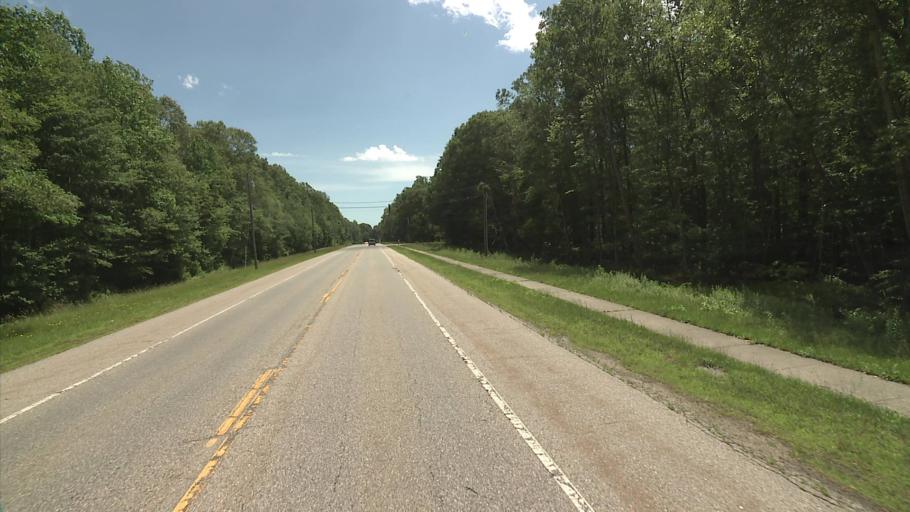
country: US
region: Connecticut
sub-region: New London County
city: Mystic
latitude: 41.3616
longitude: -71.9799
